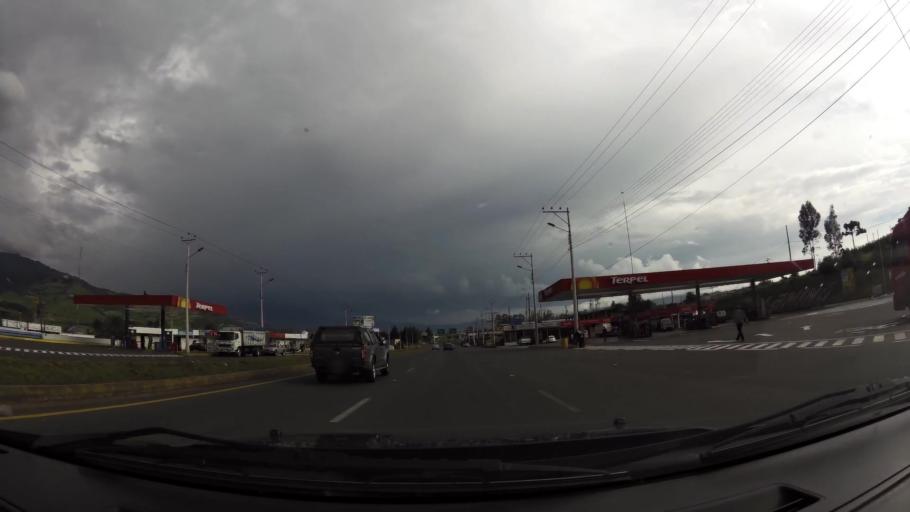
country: EC
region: Pichincha
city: Machachi
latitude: -0.4080
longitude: -78.5471
